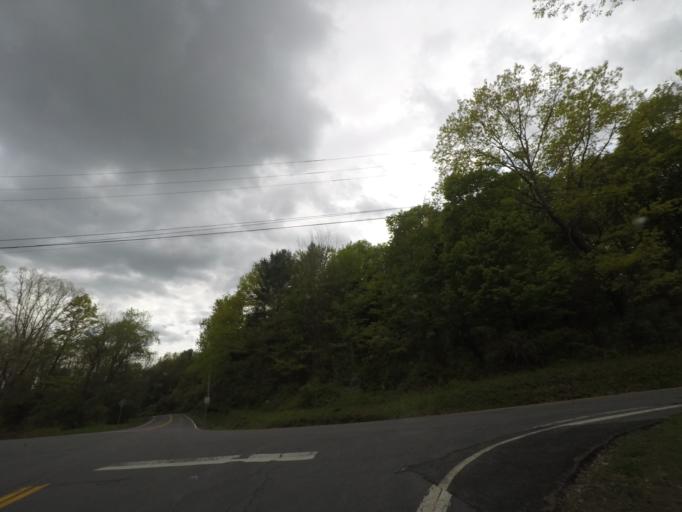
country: US
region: New York
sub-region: Albany County
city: Voorheesville
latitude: 42.6861
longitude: -73.9333
